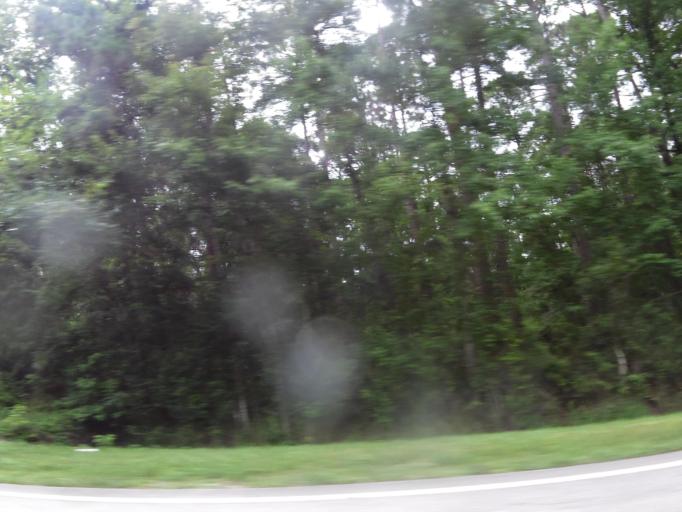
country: US
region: Florida
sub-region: Saint Johns County
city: Saint Augustine
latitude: 29.8718
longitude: -81.3692
